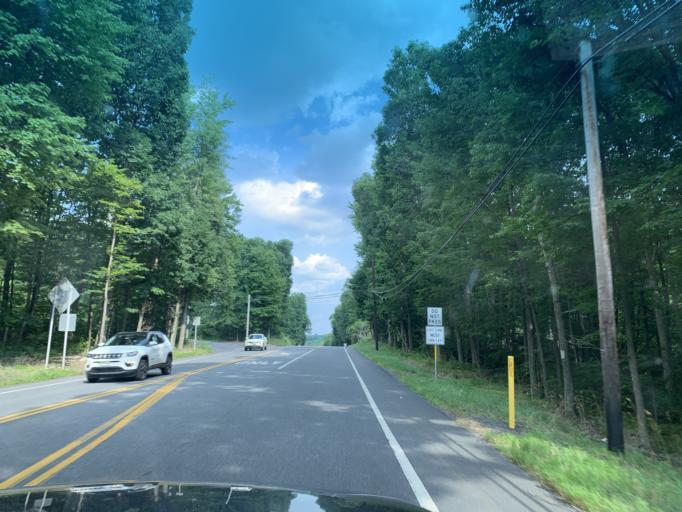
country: US
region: Pennsylvania
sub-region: Schuylkill County
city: Frackville
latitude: 40.7818
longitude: -76.2566
